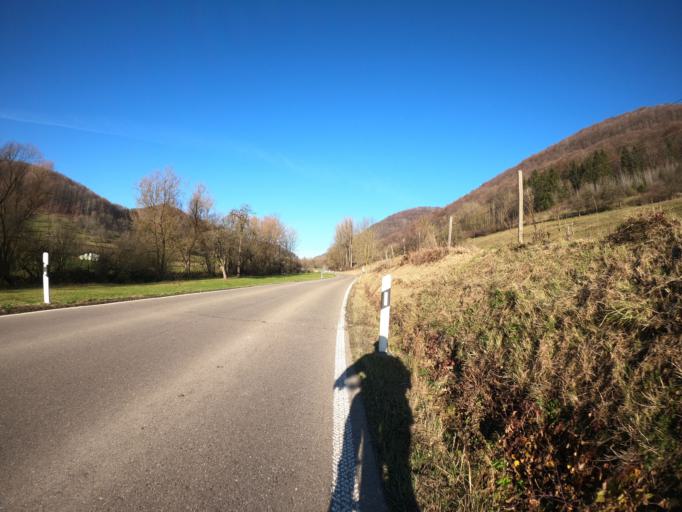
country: DE
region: Baden-Wuerttemberg
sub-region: Regierungsbezirk Stuttgart
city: Bad Ditzenbach
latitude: 48.6036
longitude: 9.6826
